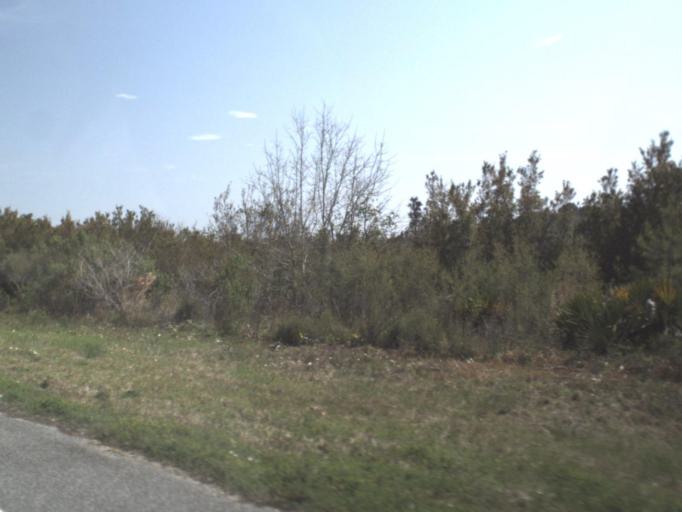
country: US
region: Florida
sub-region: Franklin County
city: Apalachicola
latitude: 29.7221
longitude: -85.0721
